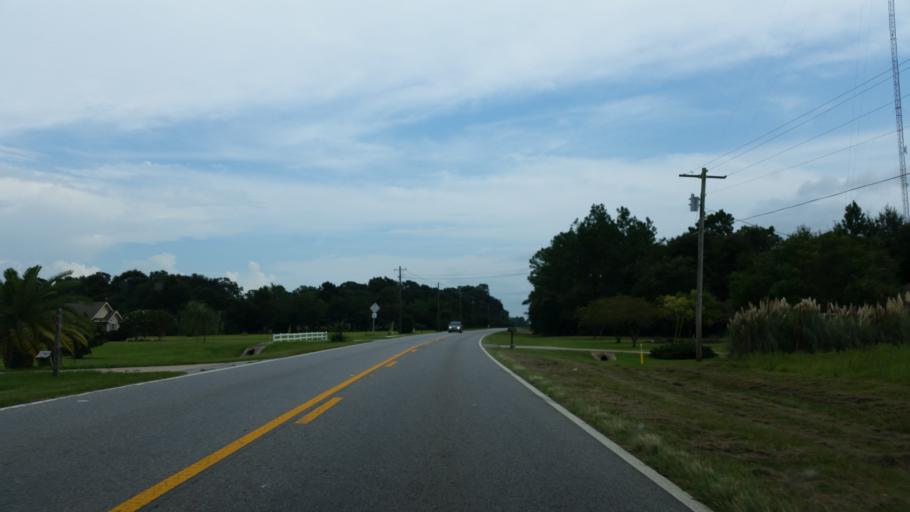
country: US
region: Florida
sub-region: Santa Rosa County
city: Wallace
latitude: 30.6600
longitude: -87.1956
